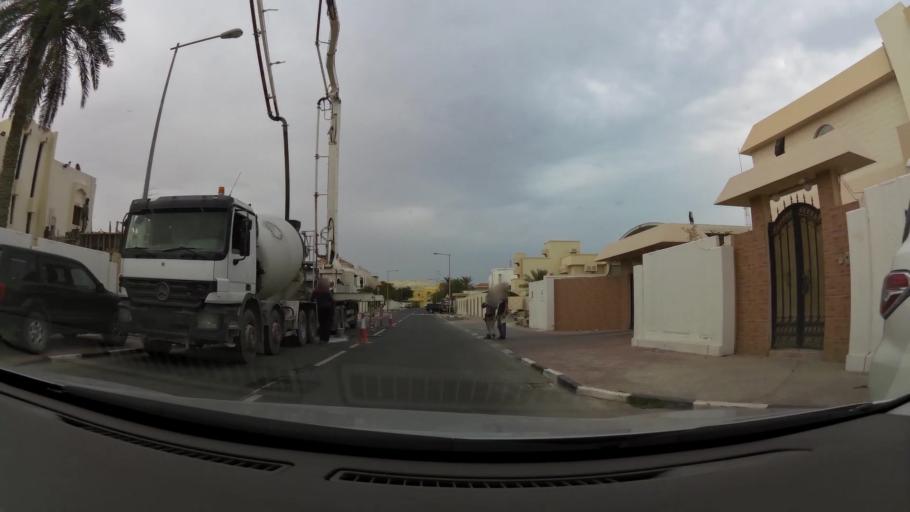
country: QA
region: Baladiyat ad Dawhah
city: Doha
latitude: 25.3332
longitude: 51.5102
